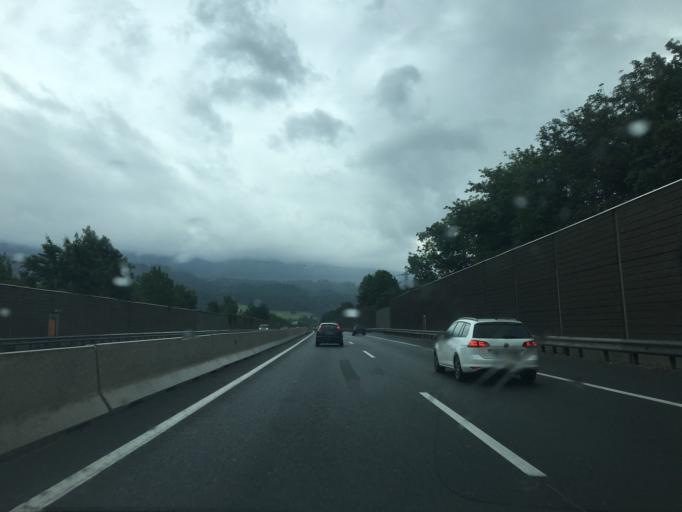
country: AT
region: Tyrol
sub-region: Politischer Bezirk Innsbruck Land
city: Volders
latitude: 47.2883
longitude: 11.5596
